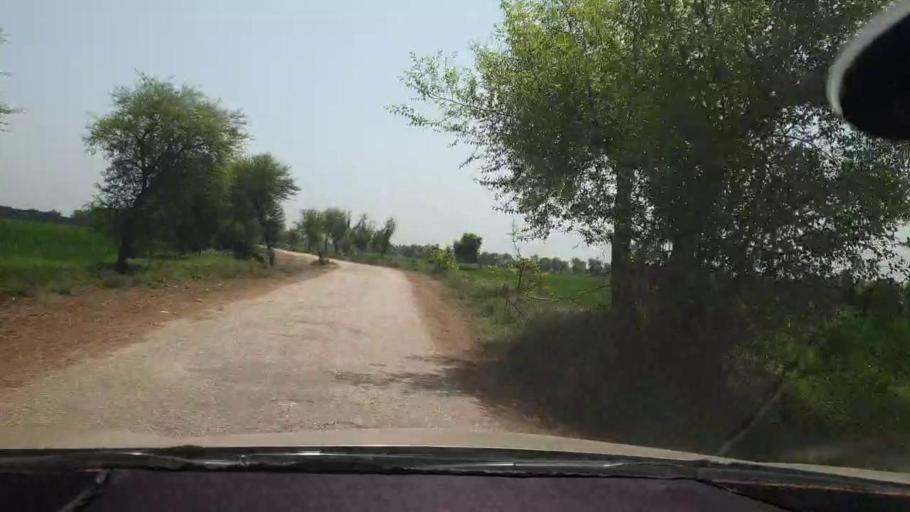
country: PK
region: Sindh
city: Kambar
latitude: 27.6803
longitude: 67.9397
